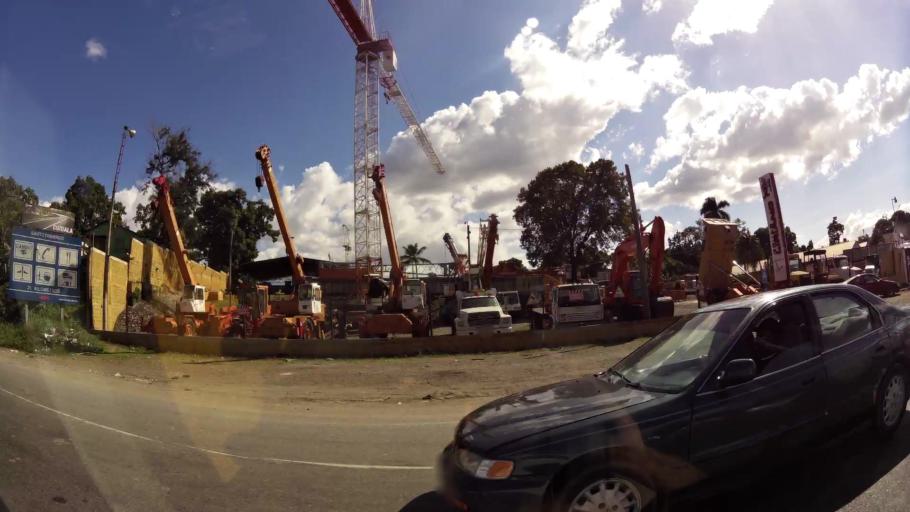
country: DO
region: Santo Domingo
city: Santo Domingo Oeste
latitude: 18.5488
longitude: -70.0460
